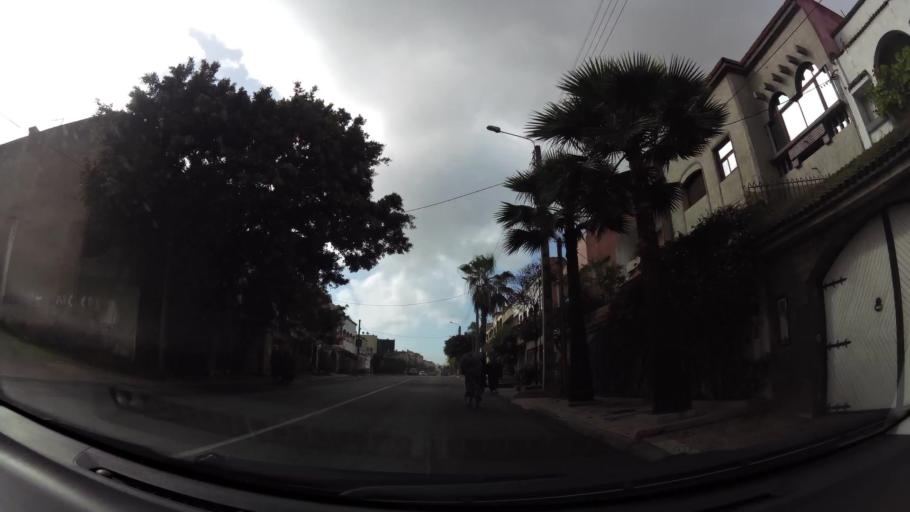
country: MA
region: Grand Casablanca
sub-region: Casablanca
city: Casablanca
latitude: 33.5652
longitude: -7.6765
